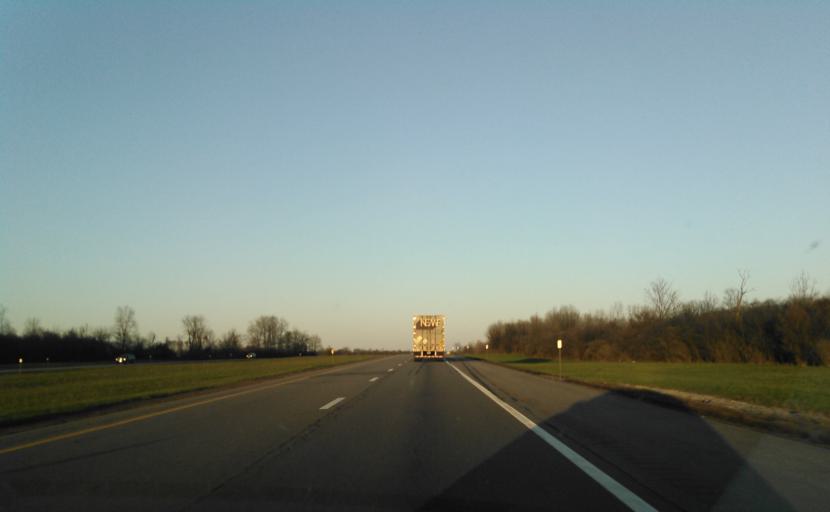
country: US
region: New York
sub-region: Ontario County
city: Clifton Springs
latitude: 42.9740
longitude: -77.1056
